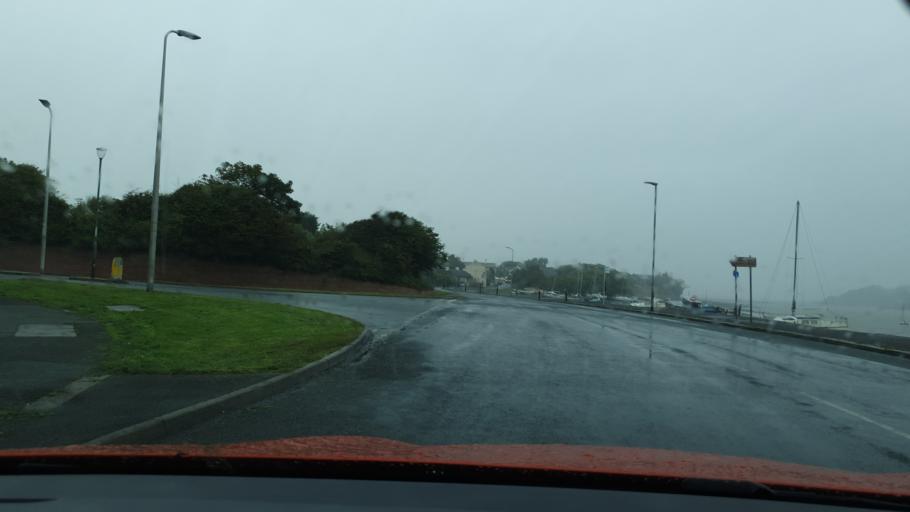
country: GB
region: England
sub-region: Cumbria
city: Barrow in Furness
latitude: 54.1144
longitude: -3.2507
